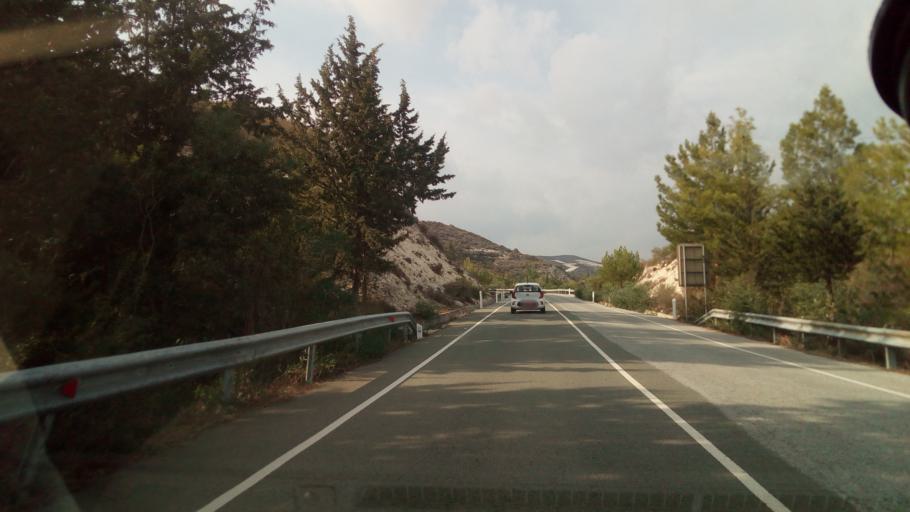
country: CY
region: Larnaka
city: Kofinou
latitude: 34.8305
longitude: 33.3546
